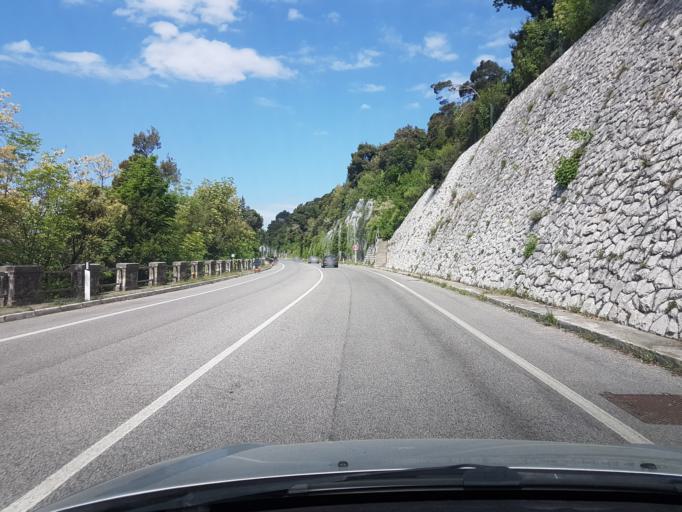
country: IT
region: Friuli Venezia Giulia
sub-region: Provincia di Trieste
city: Aurisina
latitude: 45.7400
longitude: 13.6748
